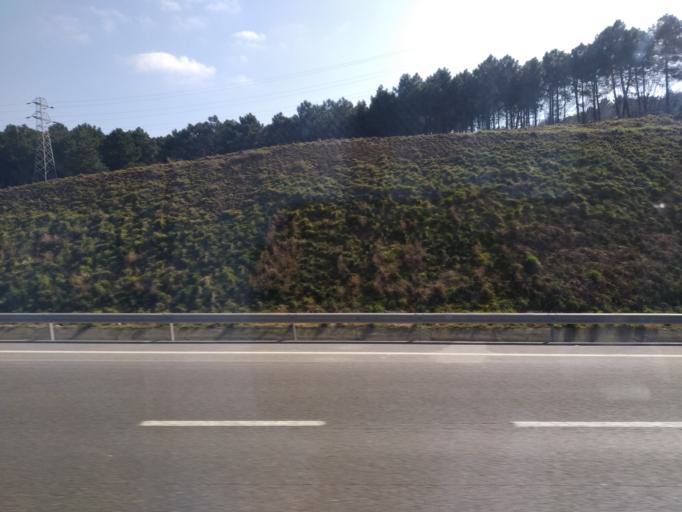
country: TR
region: Istanbul
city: Arikoey
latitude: 41.2230
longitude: 29.0132
